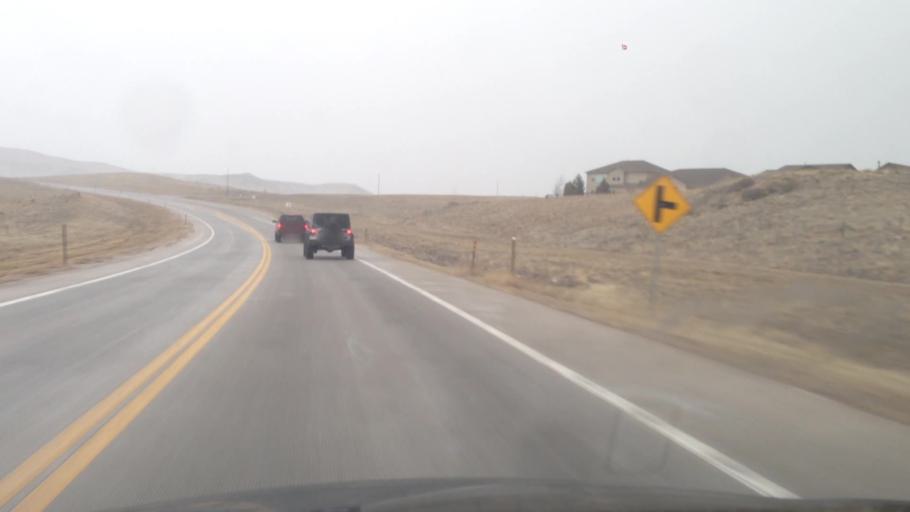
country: US
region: Colorado
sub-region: Douglas County
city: Stonegate
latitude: 39.4994
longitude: -104.8203
